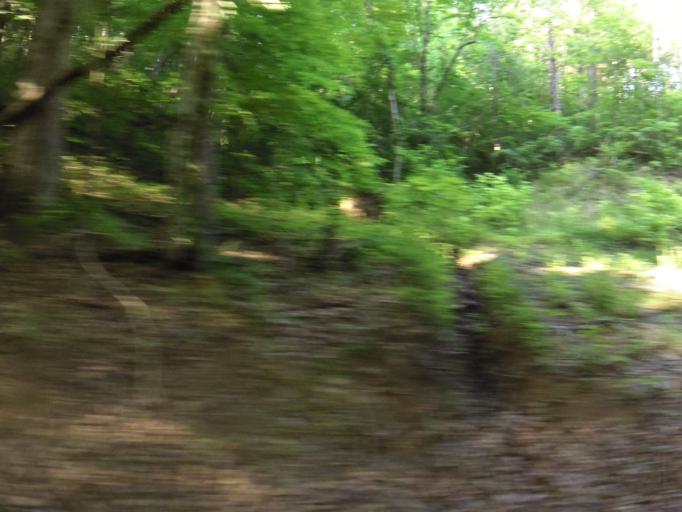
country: US
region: Tennessee
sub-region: Sevier County
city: Sevierville
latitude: 35.8542
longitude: -83.6281
